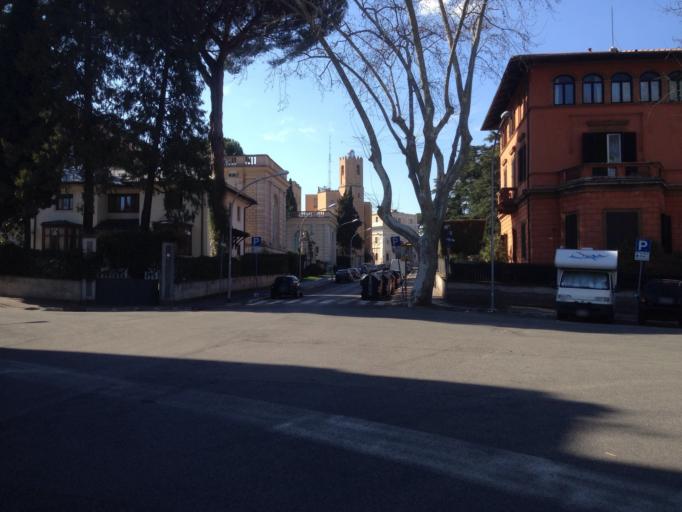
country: VA
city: Vatican City
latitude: 41.8879
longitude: 12.4640
